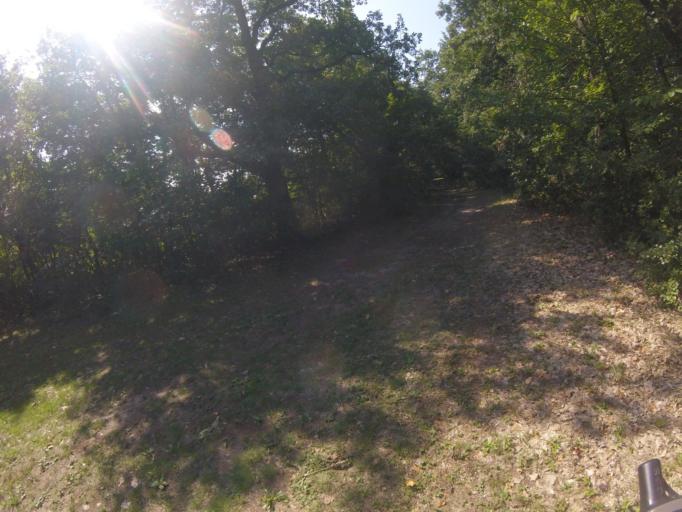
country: HU
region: Nograd
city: Bujak
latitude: 47.8871
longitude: 19.5305
